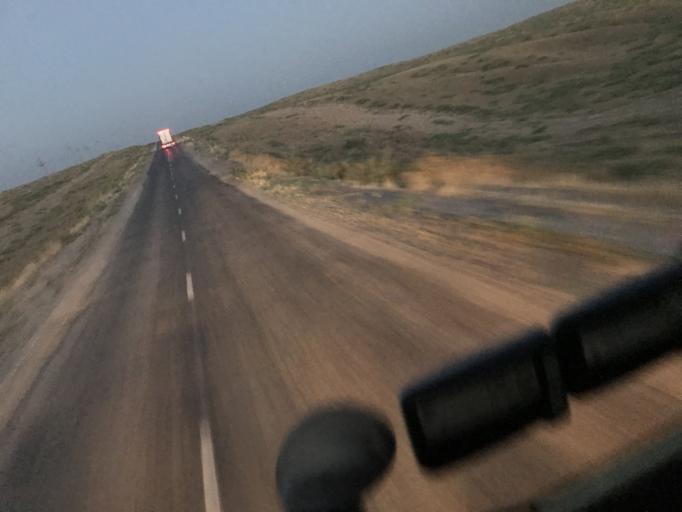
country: UZ
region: Toshkent
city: Chinoz
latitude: 41.1395
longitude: 68.7057
